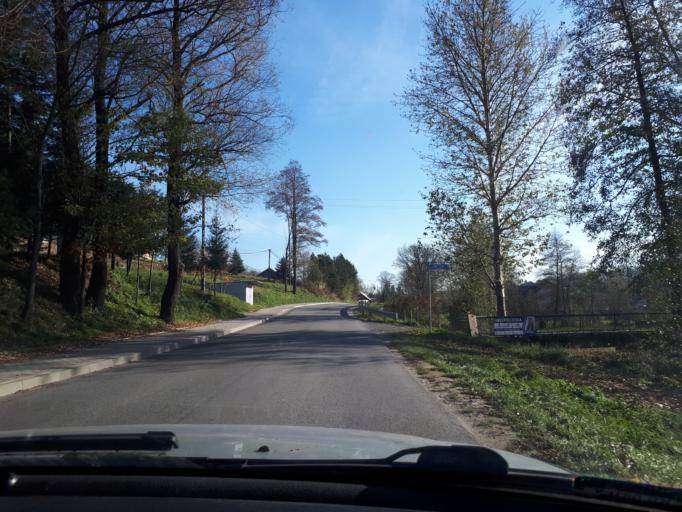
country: PL
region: Subcarpathian Voivodeship
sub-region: Powiat debicki
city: Debica
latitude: 50.0005
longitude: 21.4130
